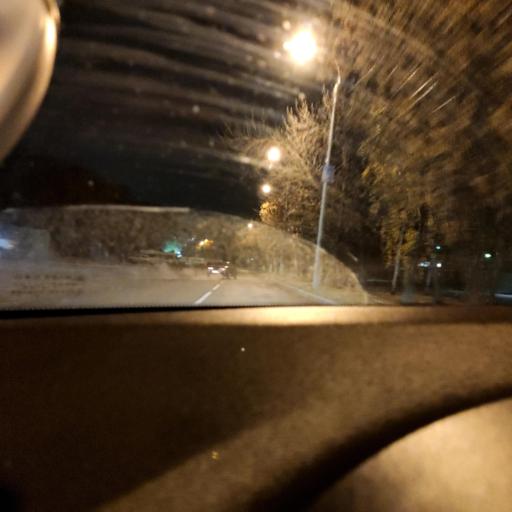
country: RU
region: Samara
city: Samara
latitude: 53.1853
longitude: 50.1726
